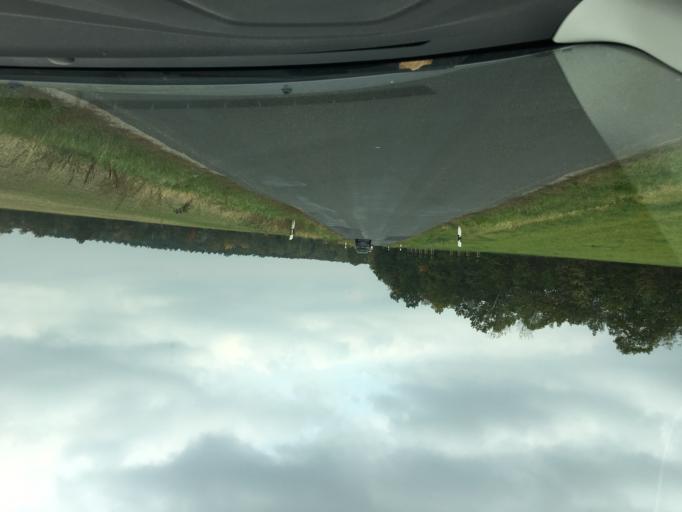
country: DE
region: Saxony
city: Bannewitz
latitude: 50.9909
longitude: 13.6822
